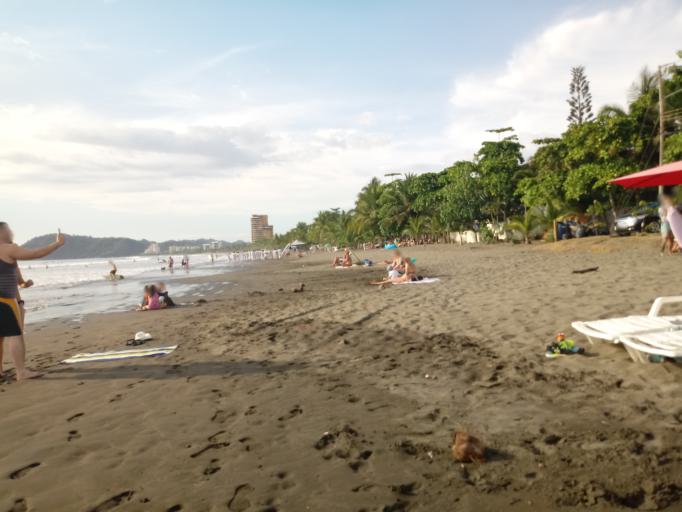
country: CR
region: Puntarenas
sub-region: Canton de Garabito
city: Jaco
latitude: 9.6028
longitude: -84.6217
